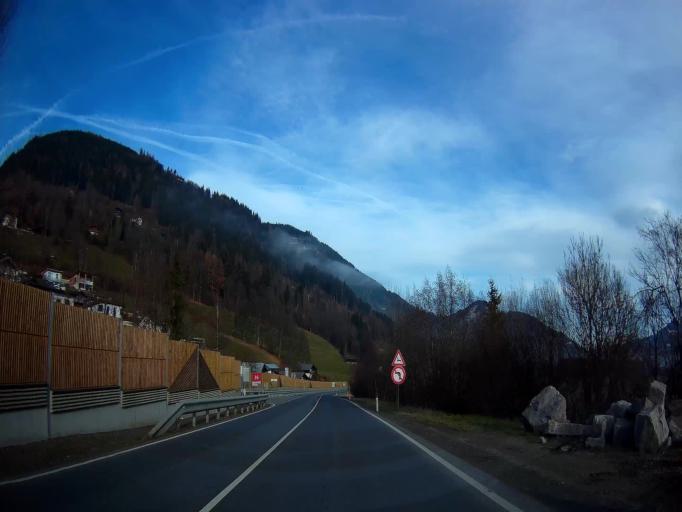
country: AT
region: Salzburg
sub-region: Politischer Bezirk Zell am See
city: Kaprun
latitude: 47.2907
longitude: 12.7469
